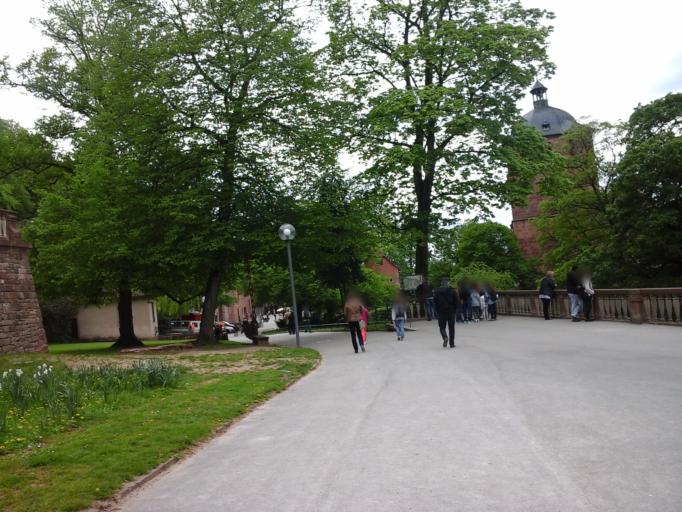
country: DE
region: Baden-Wuerttemberg
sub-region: Karlsruhe Region
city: Heidelberg
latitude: 49.4100
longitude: 8.7169
